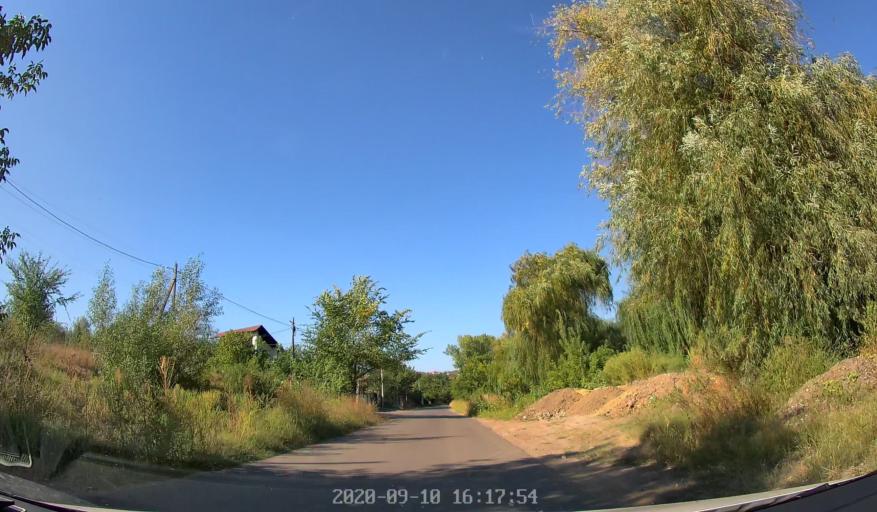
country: MD
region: Chisinau
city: Stauceni
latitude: 47.0501
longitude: 28.9253
